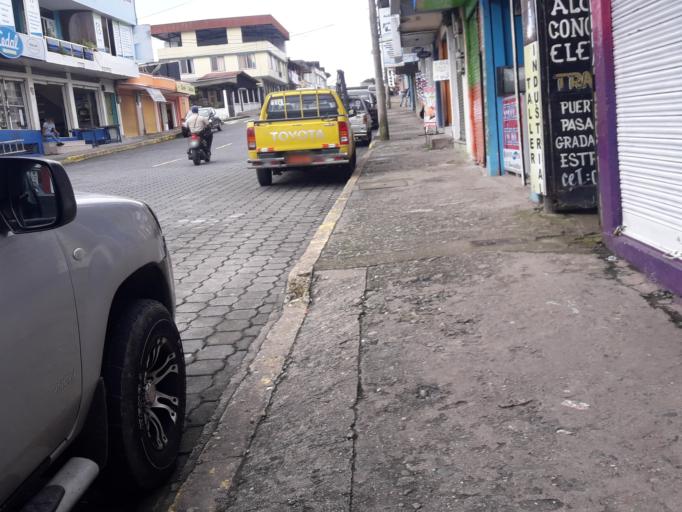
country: EC
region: Napo
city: Tena
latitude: -0.9970
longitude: -77.8132
